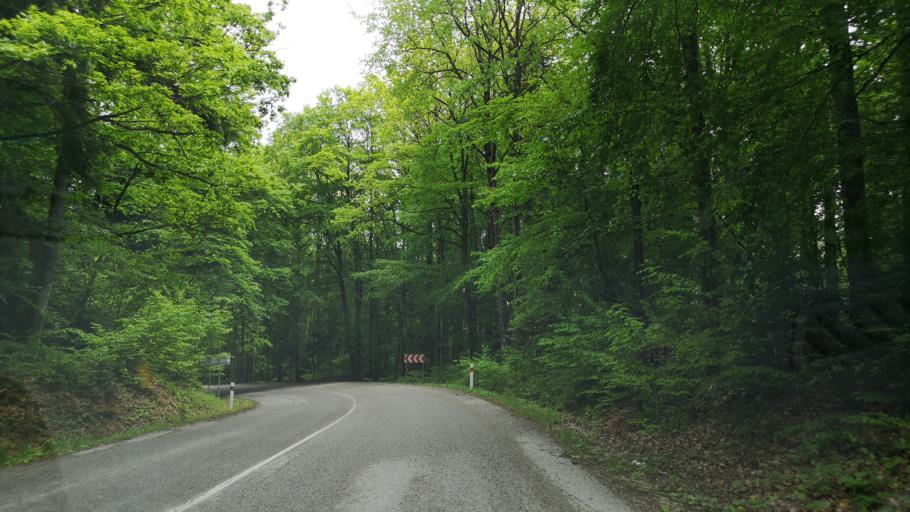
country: SK
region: Banskobystricky
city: Revuca
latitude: 48.6488
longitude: 20.2964
